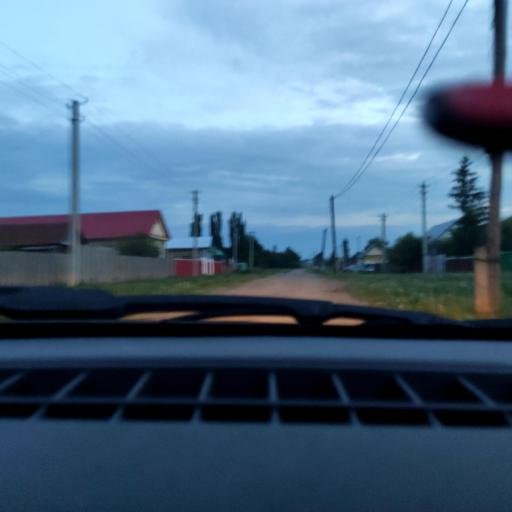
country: RU
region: Bashkortostan
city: Tolbazy
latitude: 54.2897
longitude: 55.8219
